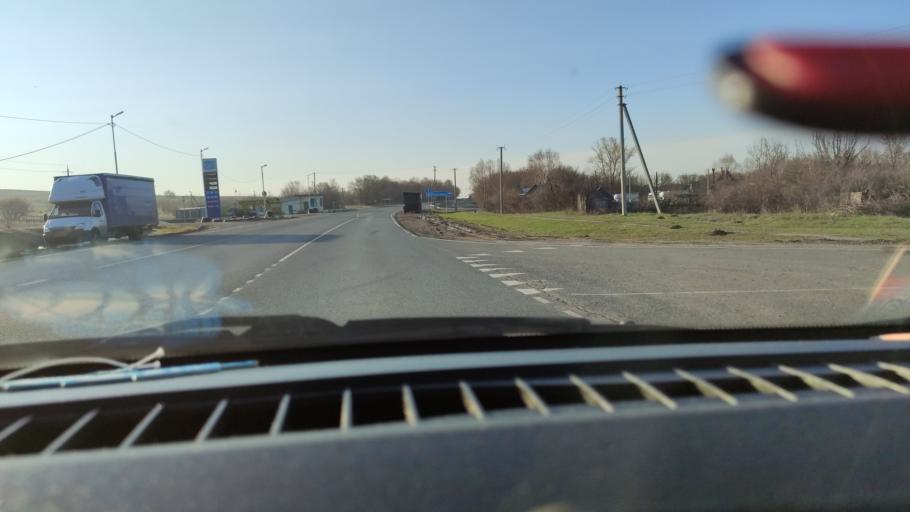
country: RU
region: Saratov
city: Tersa
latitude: 52.0943
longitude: 47.5410
